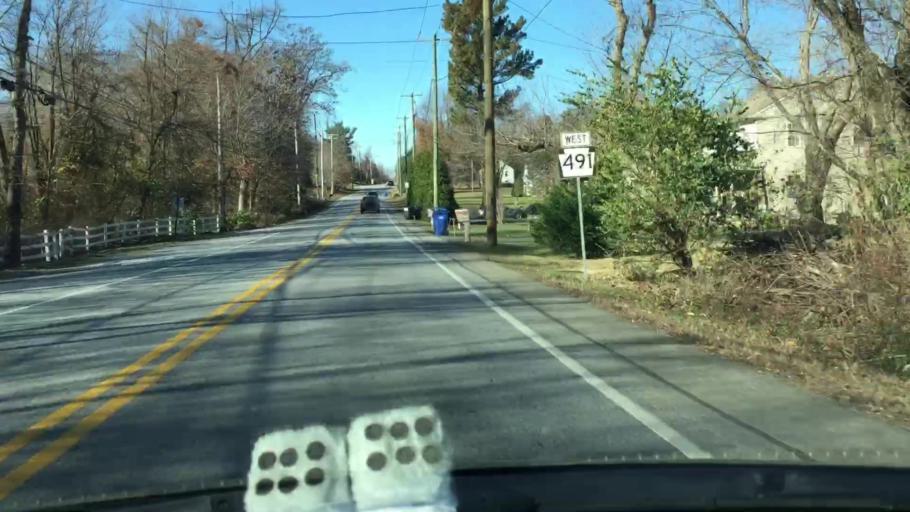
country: US
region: Pennsylvania
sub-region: Delaware County
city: Chester Heights
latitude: 39.8473
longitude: -75.5313
